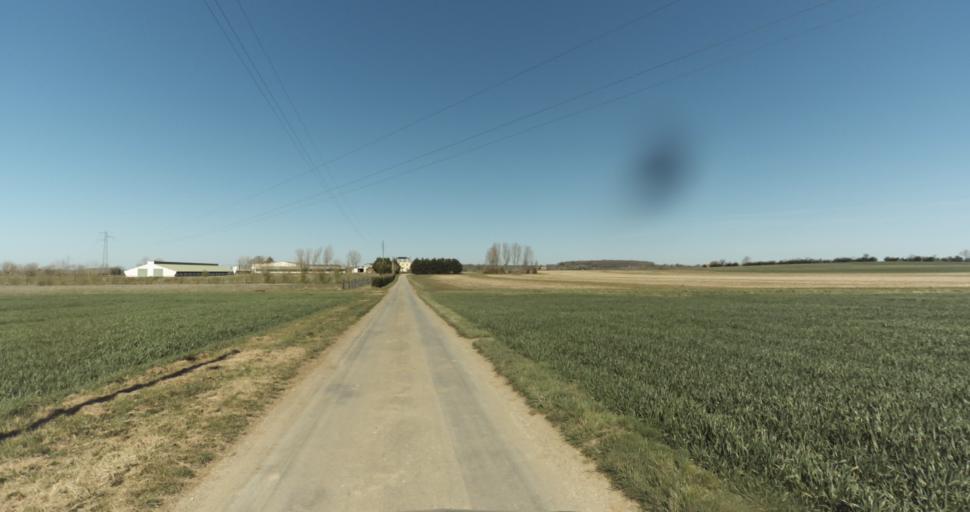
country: FR
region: Lower Normandy
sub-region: Departement du Calvados
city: Saint-Pierre-sur-Dives
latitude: 49.0208
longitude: 0.0318
